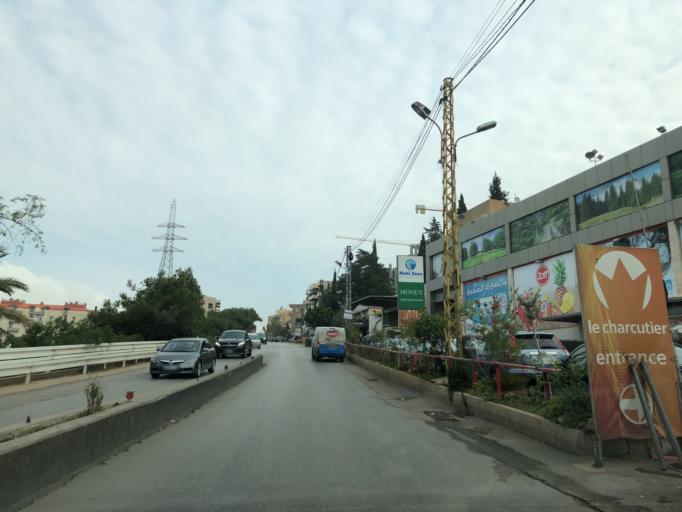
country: LB
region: Mont-Liban
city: Jdaidet el Matn
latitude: 33.8536
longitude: 35.5814
